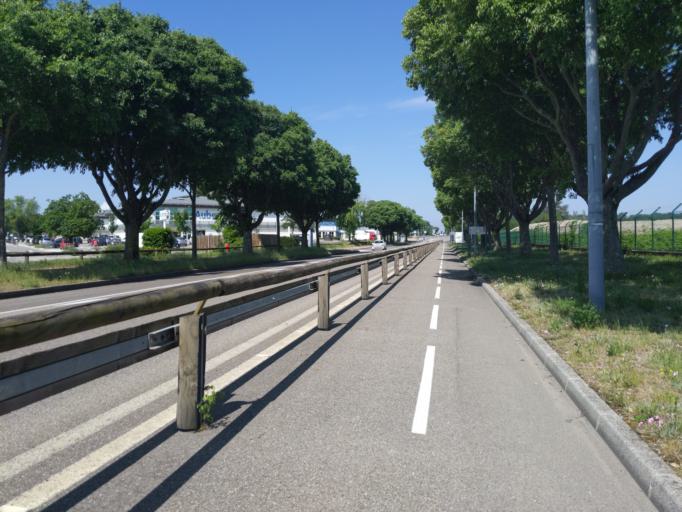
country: FR
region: Rhone-Alpes
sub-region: Departement du Rhone
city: Bron
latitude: 45.7257
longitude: 4.9321
